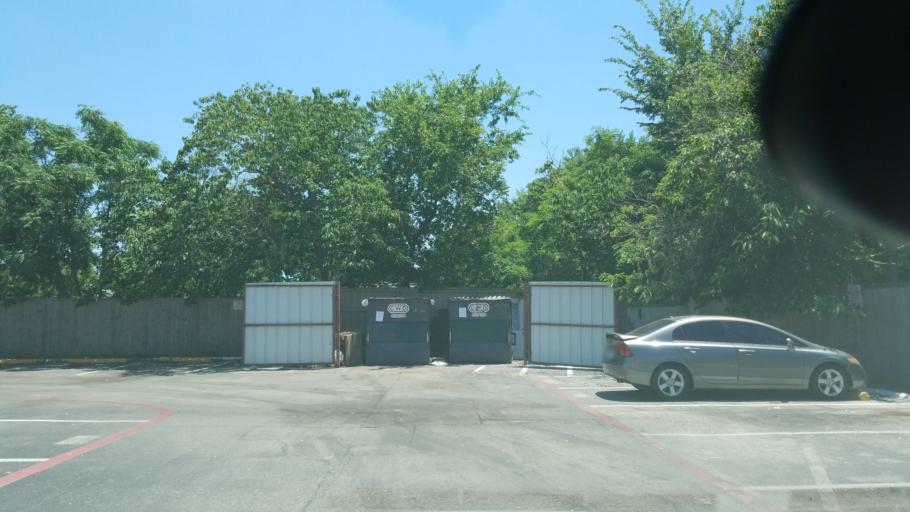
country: US
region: Texas
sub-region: Dallas County
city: Irving
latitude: 32.8264
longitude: -96.9368
